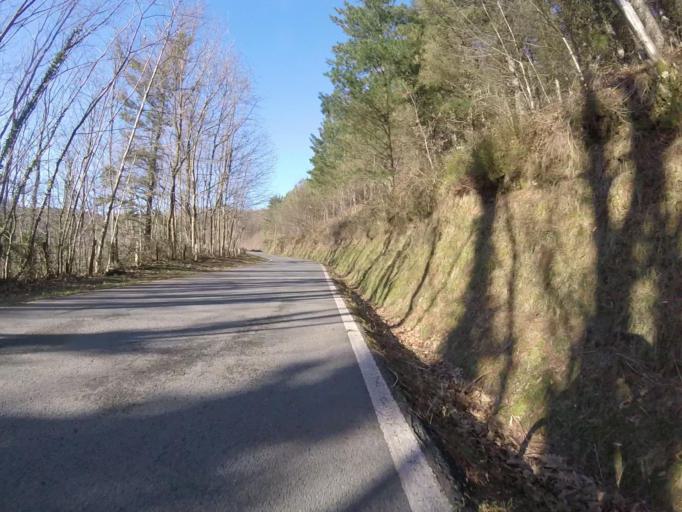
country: ES
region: Navarre
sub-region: Provincia de Navarra
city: Lesaka
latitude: 43.2622
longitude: -1.7376
